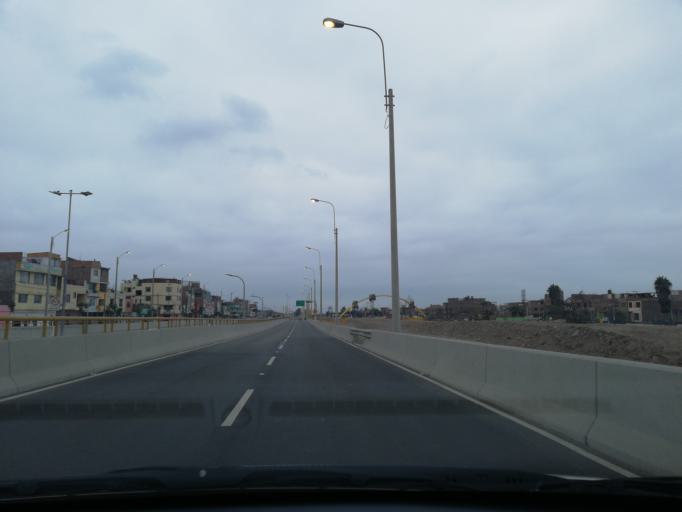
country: PE
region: Lima
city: Lima
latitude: -12.0352
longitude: -77.0750
